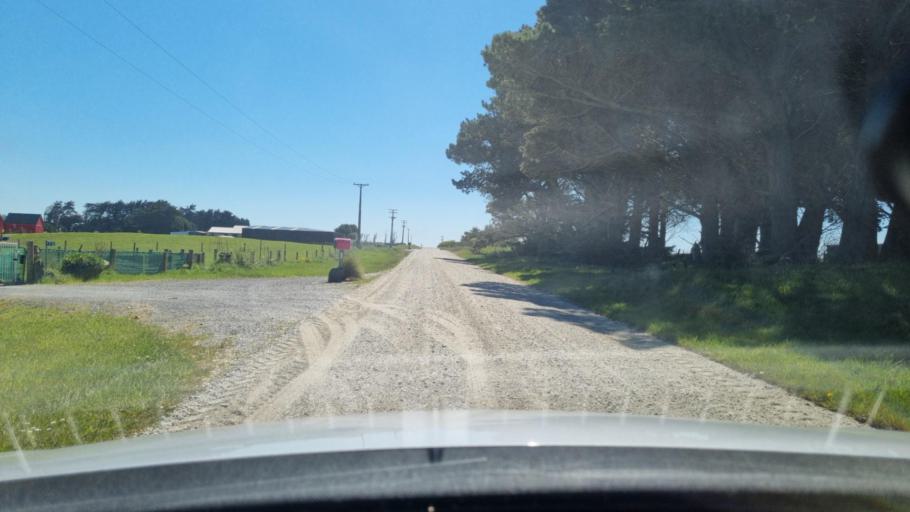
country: NZ
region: Southland
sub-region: Invercargill City
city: Invercargill
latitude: -46.4135
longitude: 168.2634
